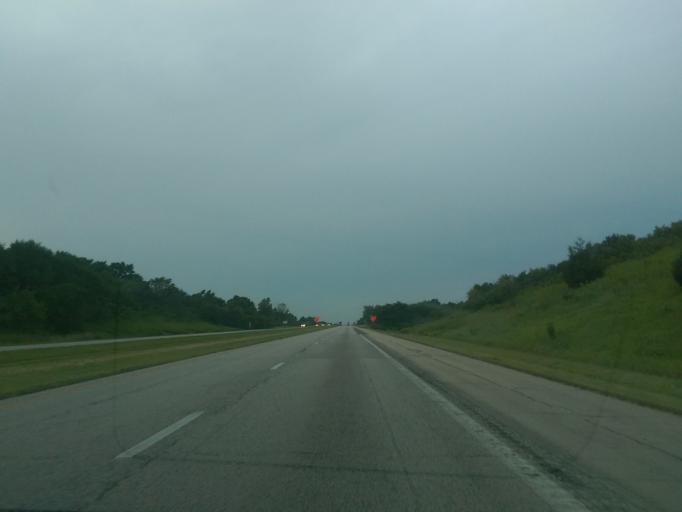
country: US
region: Missouri
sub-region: Holt County
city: Oregon
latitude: 40.0356
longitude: -95.1208
